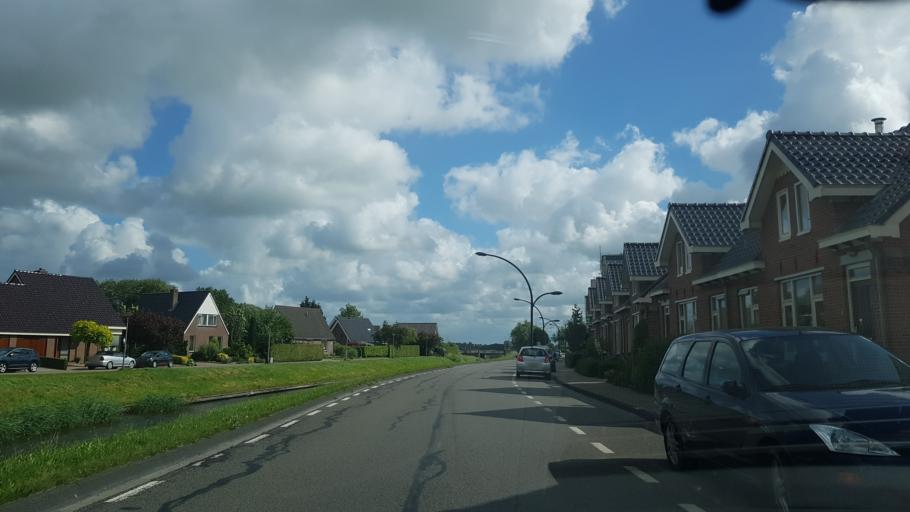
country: NL
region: Groningen
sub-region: Gemeente Bedum
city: Bedum
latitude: 53.4014
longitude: 6.6762
